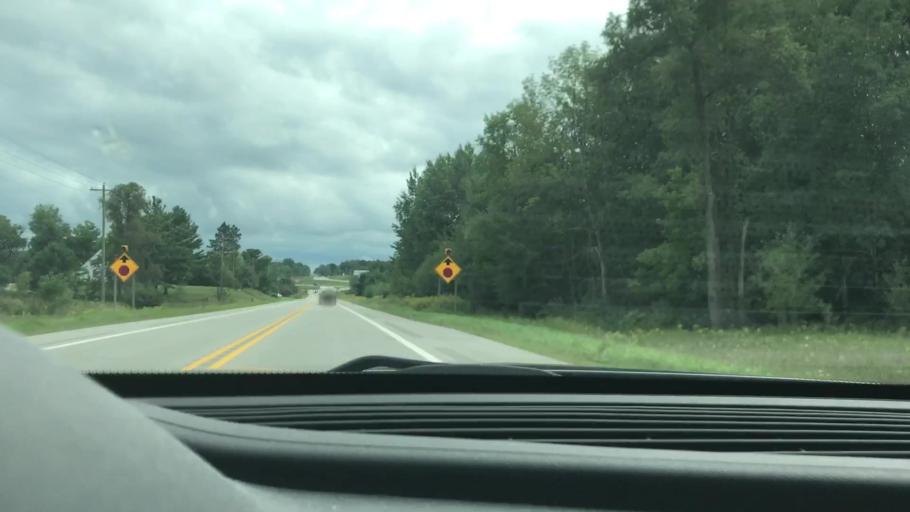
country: US
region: Michigan
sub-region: Osceola County
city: Evart
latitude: 44.0378
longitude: -85.1478
